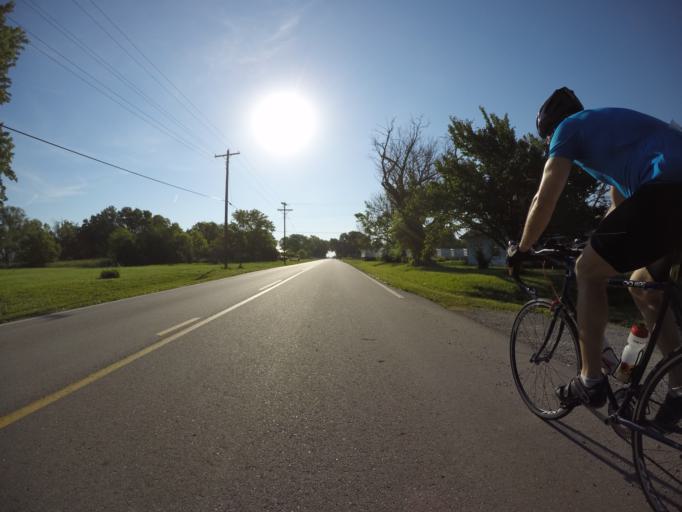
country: US
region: Nebraska
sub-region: Gage County
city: Wymore
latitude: 40.0883
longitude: -96.4841
